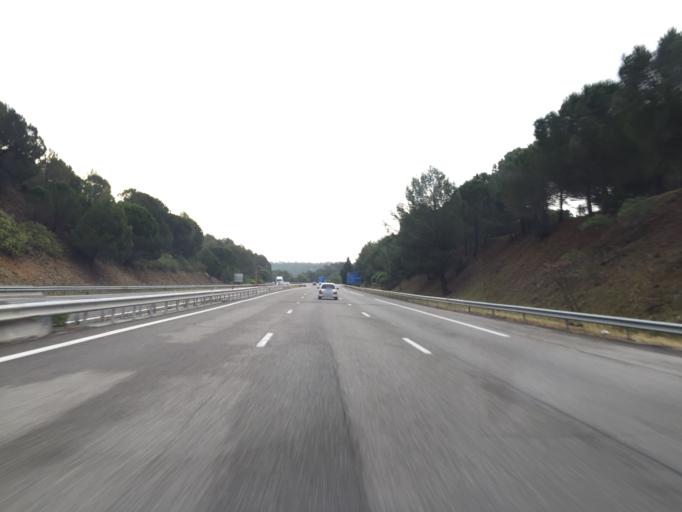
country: FR
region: Provence-Alpes-Cote d'Azur
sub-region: Departement du Var
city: Le Val
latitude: 43.4208
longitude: 6.0772
